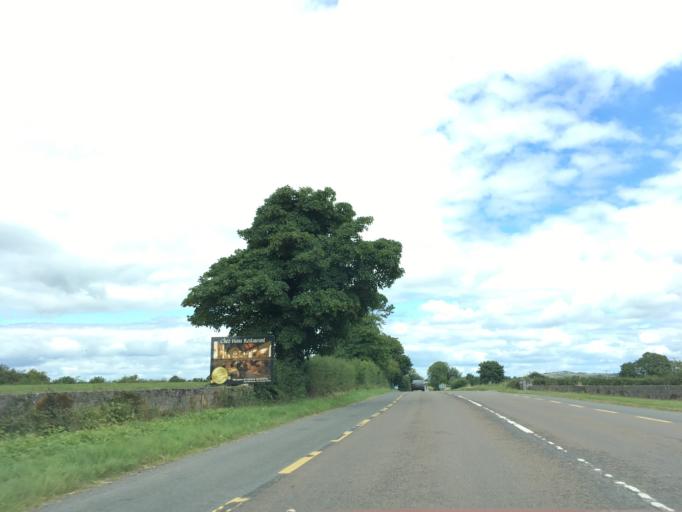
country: IE
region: Munster
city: Cashel
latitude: 52.4917
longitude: -7.8902
